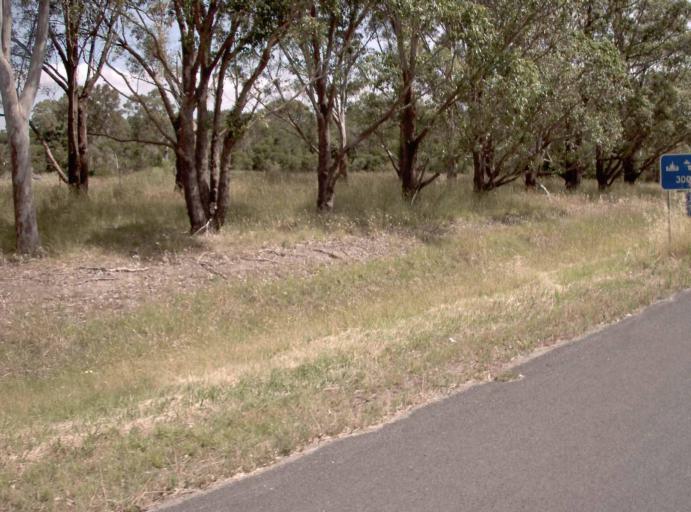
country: AU
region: Victoria
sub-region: Wellington
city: Heyfield
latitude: -38.1530
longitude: 146.7673
